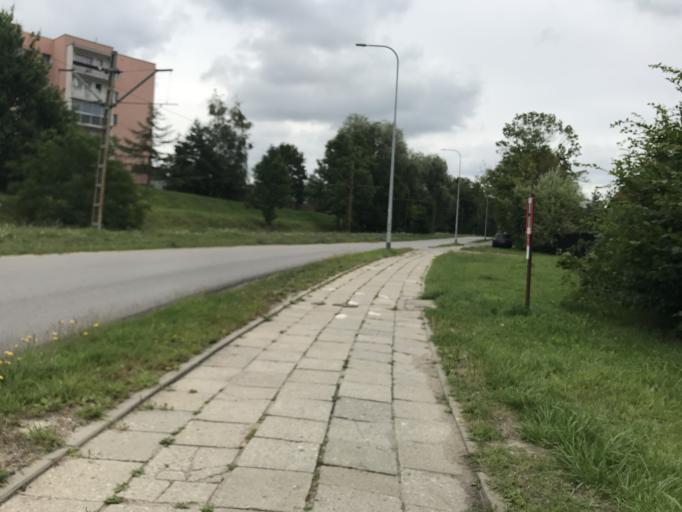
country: PL
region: Warmian-Masurian Voivodeship
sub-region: Powiat elblaski
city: Elblag
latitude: 54.1774
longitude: 19.4306
